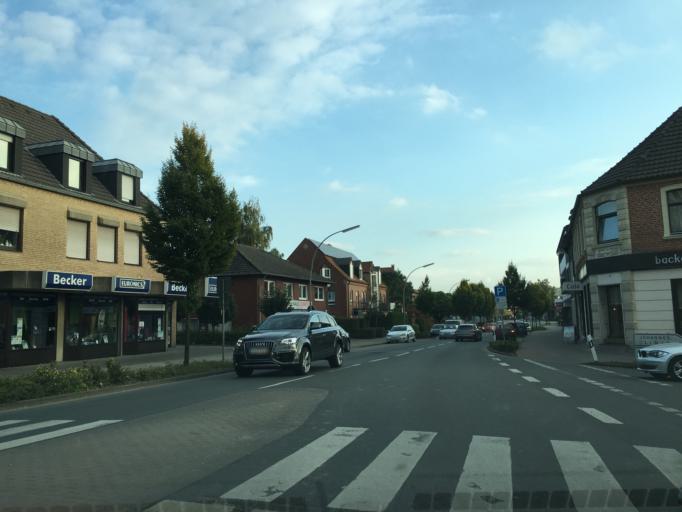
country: DE
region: North Rhine-Westphalia
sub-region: Regierungsbezirk Munster
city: Altenberge
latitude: 52.0456
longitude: 7.4654
